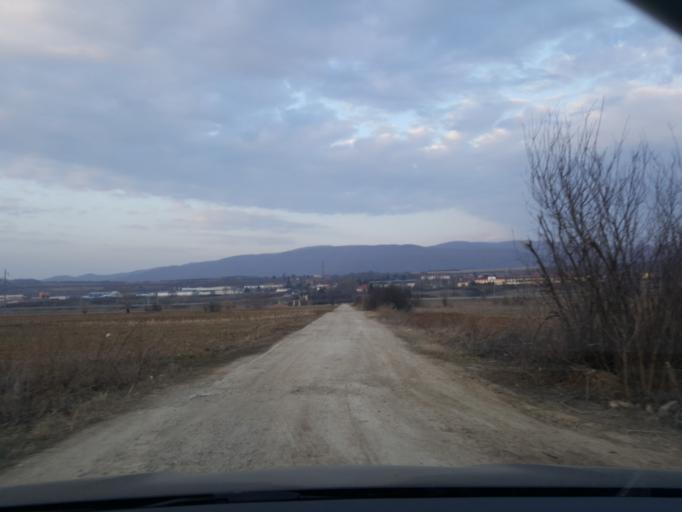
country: RS
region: Central Serbia
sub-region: Nisavski Okrug
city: Aleksinac
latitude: 43.5487
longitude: 21.6795
